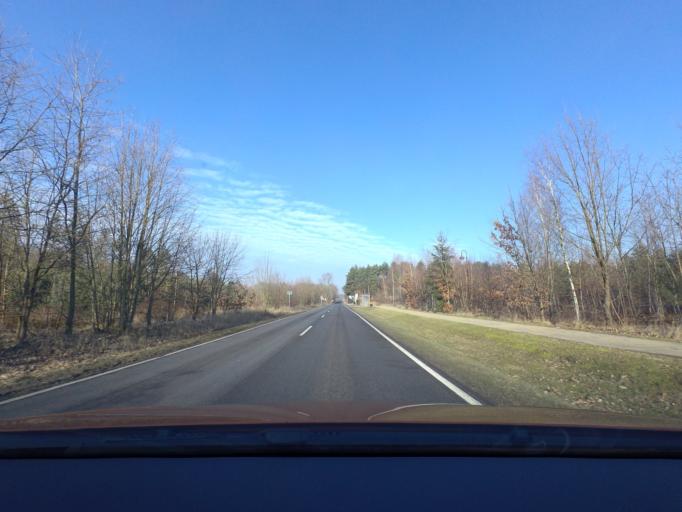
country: DE
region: Brandenburg
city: Liebenwalde
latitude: 52.8363
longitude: 13.4077
